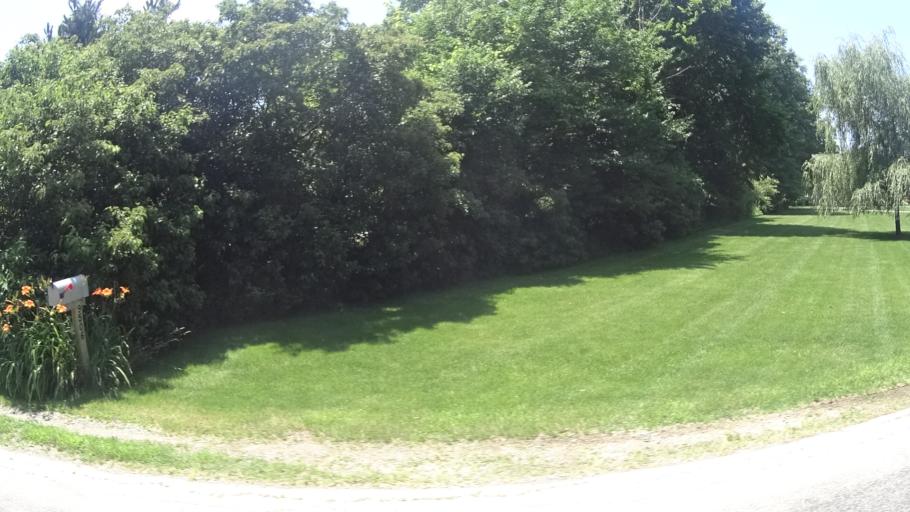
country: US
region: Ohio
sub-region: Lorain County
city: Vermilion
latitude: 41.3502
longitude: -82.3917
